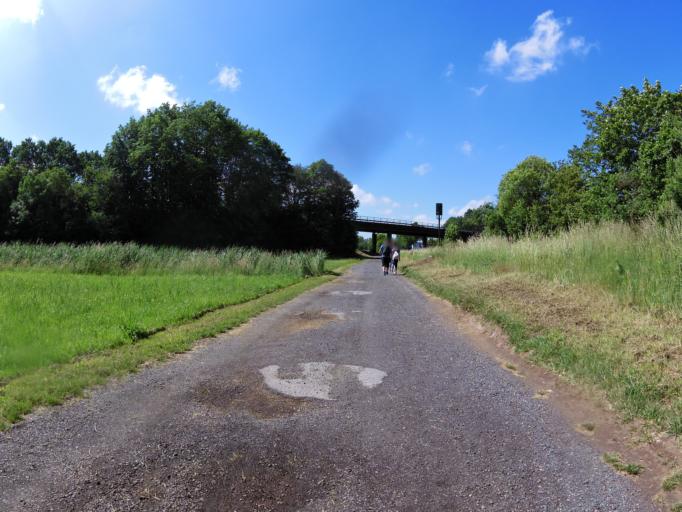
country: DE
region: Hesse
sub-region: Regierungsbezirk Kassel
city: Bad Hersfeld
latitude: 50.8563
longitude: 9.6927
